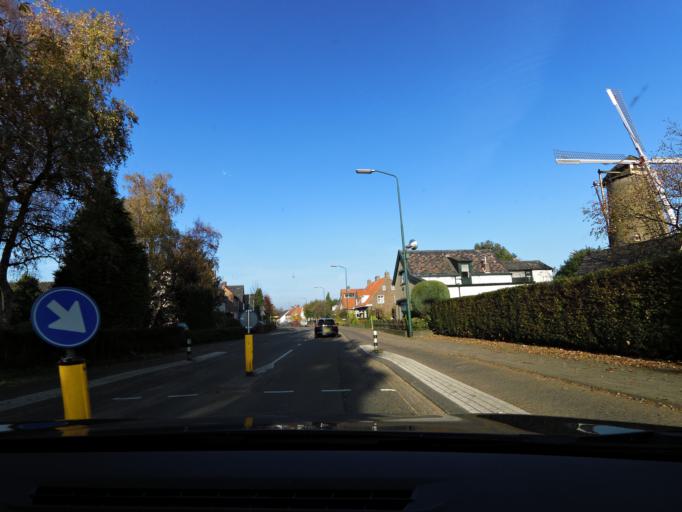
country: NL
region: North Brabant
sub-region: Gemeente Breda
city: Breda
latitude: 51.5457
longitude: 4.7972
